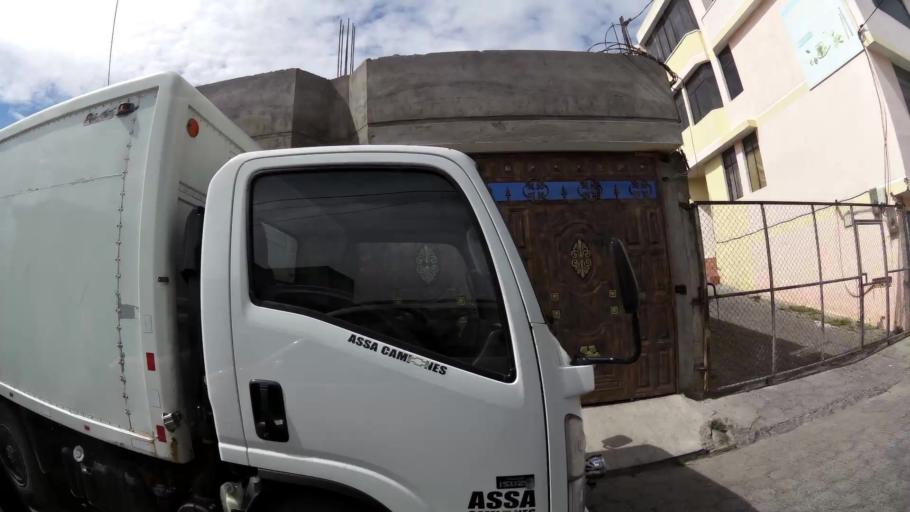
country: EC
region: Cotopaxi
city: Latacunga
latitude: -0.9285
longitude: -78.6008
